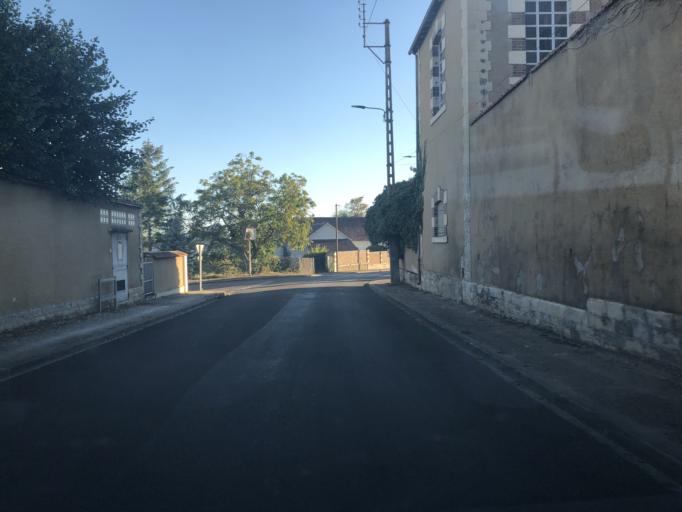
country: FR
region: Bourgogne
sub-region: Departement de l'Yonne
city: Joigny
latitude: 47.9811
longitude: 3.4066
